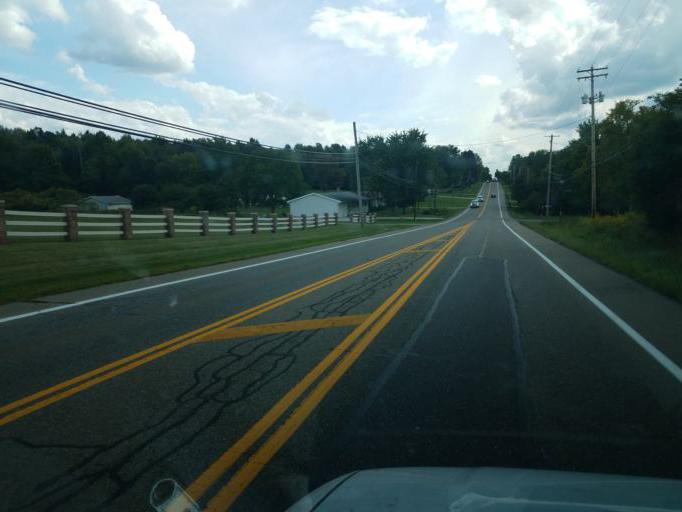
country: US
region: Ohio
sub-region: Portage County
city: Ravenna
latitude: 41.0881
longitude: -81.2430
